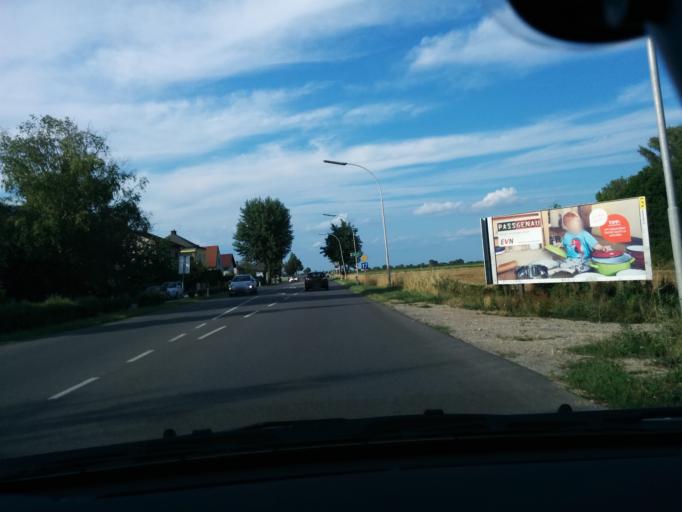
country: AT
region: Lower Austria
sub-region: Politischer Bezirk Baden
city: Gunselsdorf
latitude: 47.9472
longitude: 16.2617
